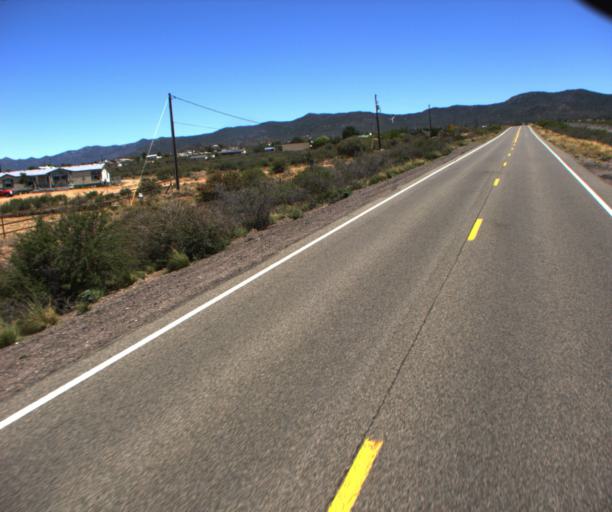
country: US
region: Arizona
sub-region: Yavapai County
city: Prescott
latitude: 34.4115
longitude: -112.6091
